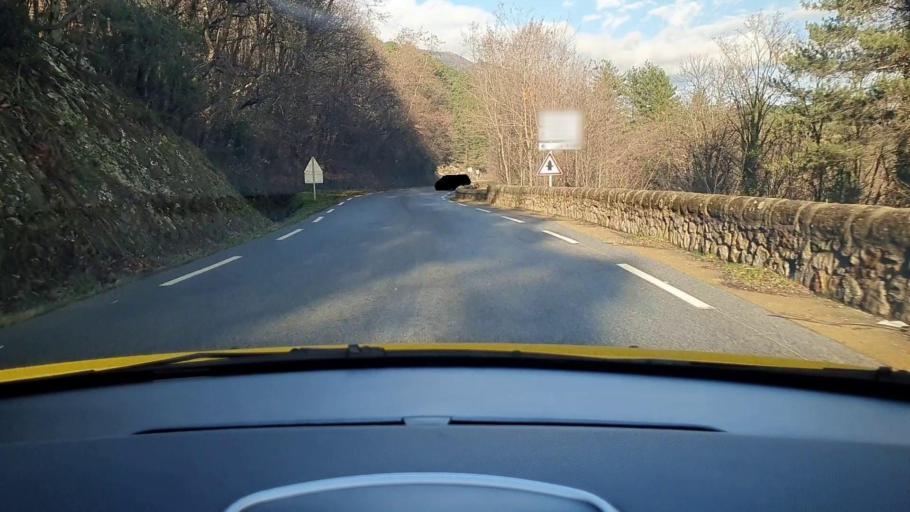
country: FR
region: Languedoc-Roussillon
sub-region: Departement du Gard
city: Branoux-les-Taillades
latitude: 44.3367
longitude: 3.9541
